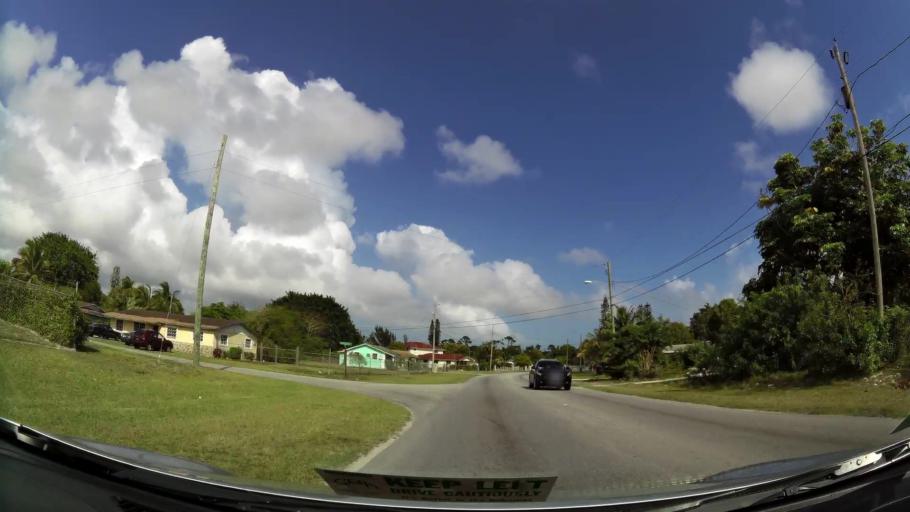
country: BS
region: Freeport
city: Freeport
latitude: 26.5266
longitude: -78.6837
